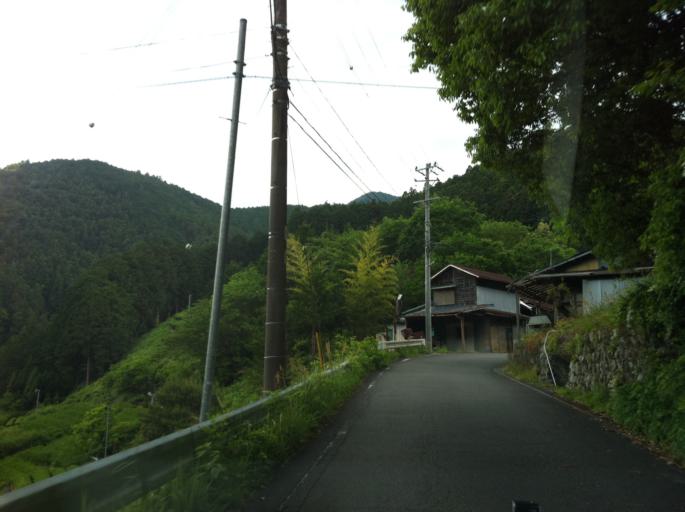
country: JP
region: Shizuoka
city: Shizuoka-shi
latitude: 35.1464
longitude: 138.3294
